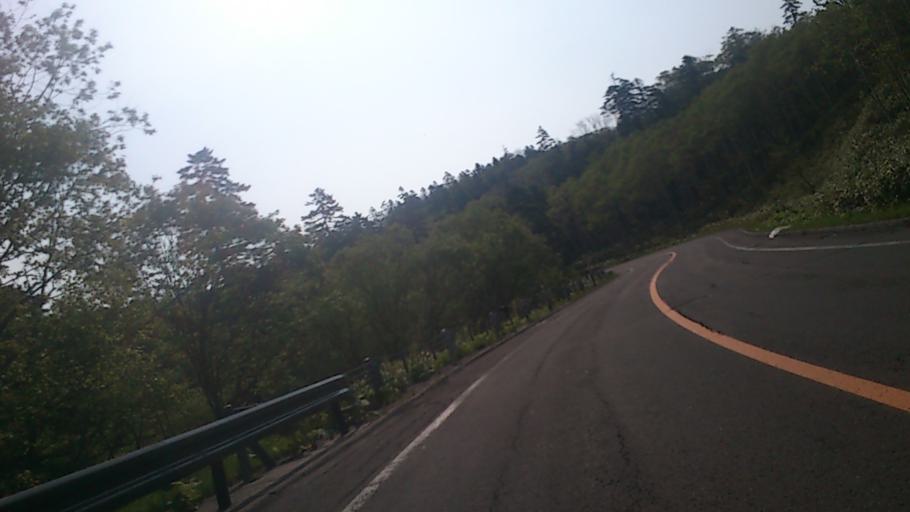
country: JP
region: Hokkaido
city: Bihoro
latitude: 43.4495
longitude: 144.2216
